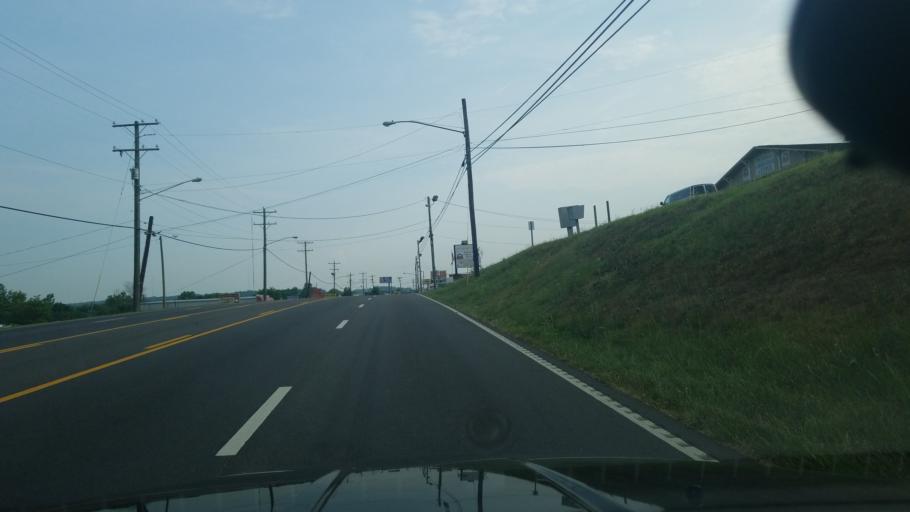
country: US
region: Tennessee
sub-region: Davidson County
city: Goodlettsville
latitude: 36.2639
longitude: -86.7571
